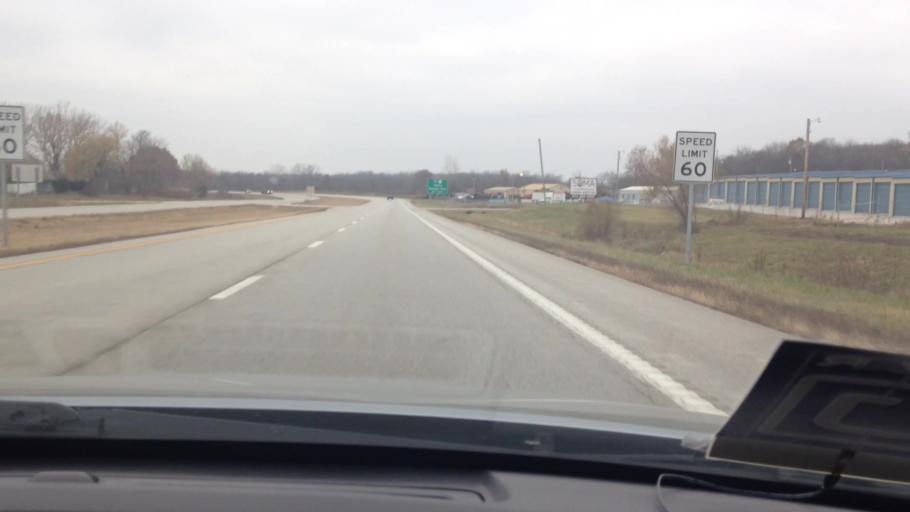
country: US
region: Missouri
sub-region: Cass County
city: Harrisonville
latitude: 38.6146
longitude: -94.3279
